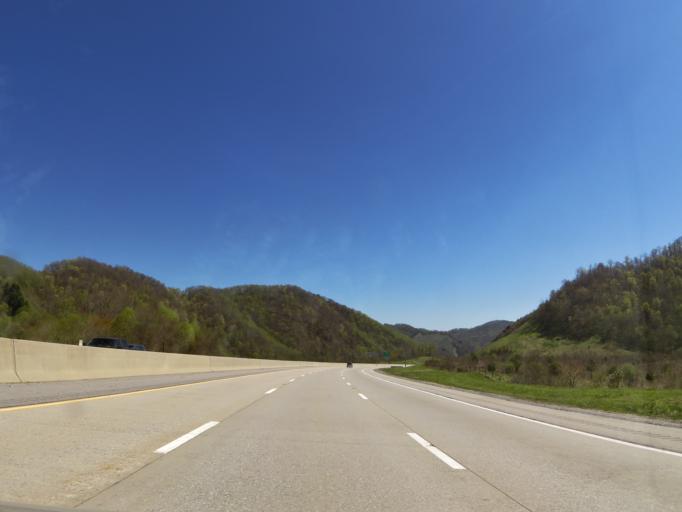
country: US
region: North Carolina
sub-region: Madison County
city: Mars Hill
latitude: 35.9323
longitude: -82.5568
